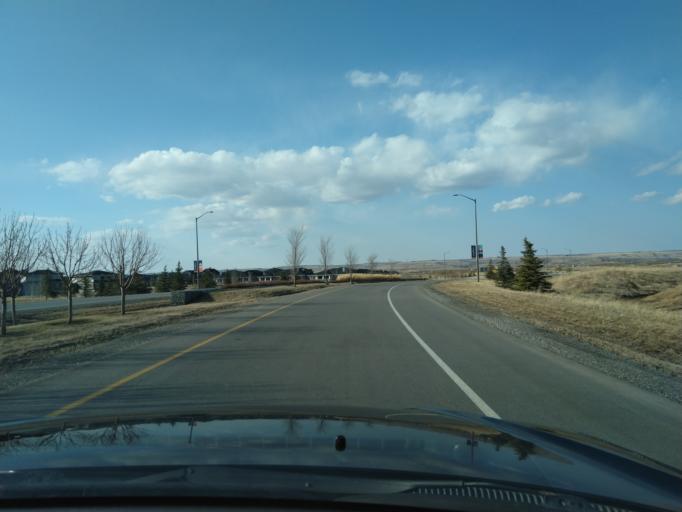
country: CA
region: Alberta
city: Cochrane
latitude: 51.1067
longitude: -114.3921
